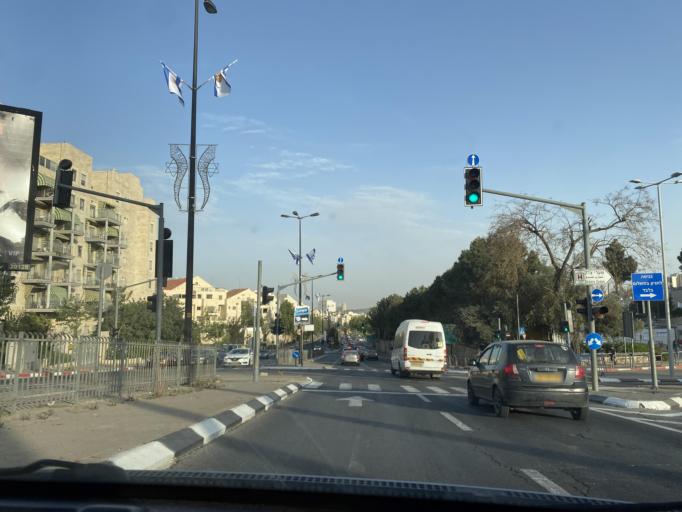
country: IL
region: Jerusalem
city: Jerusalem
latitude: 31.7750
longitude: 35.1854
